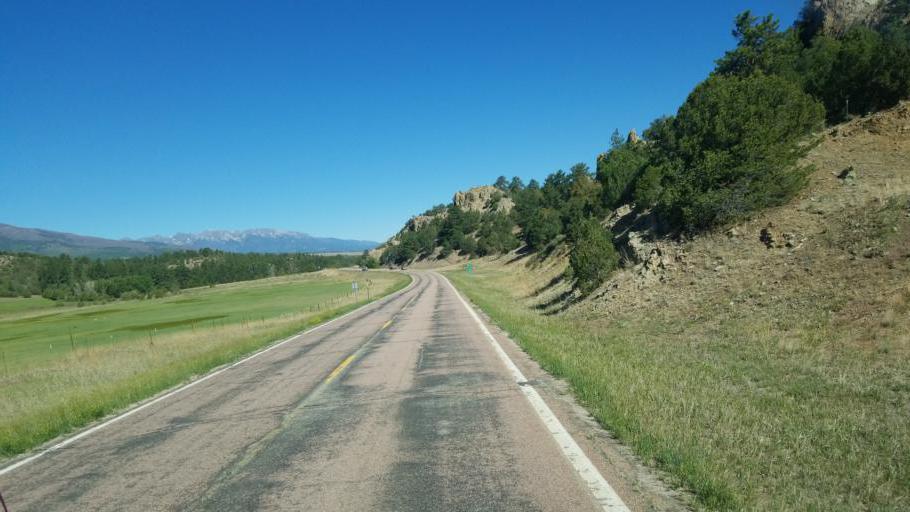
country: US
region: Colorado
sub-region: Custer County
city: Westcliffe
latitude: 38.2479
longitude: -105.5731
